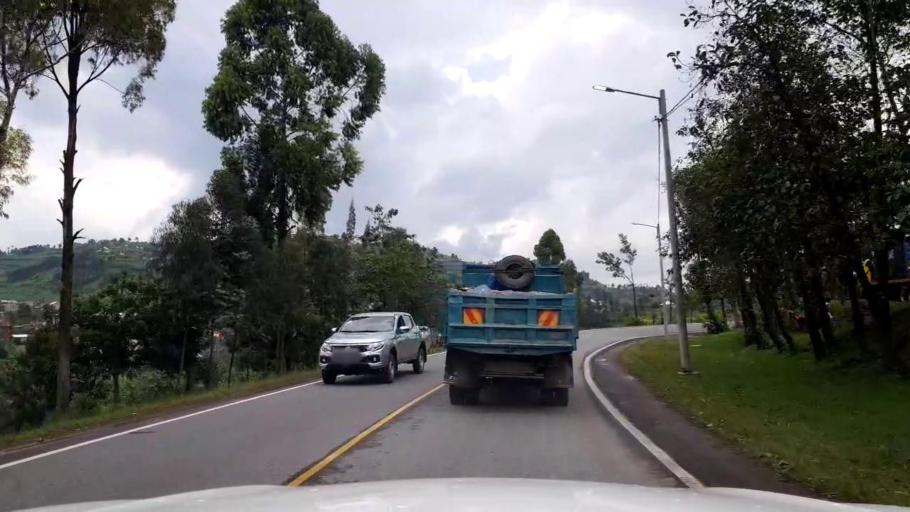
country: RW
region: Western Province
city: Gisenyi
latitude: -1.6983
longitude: 29.2716
